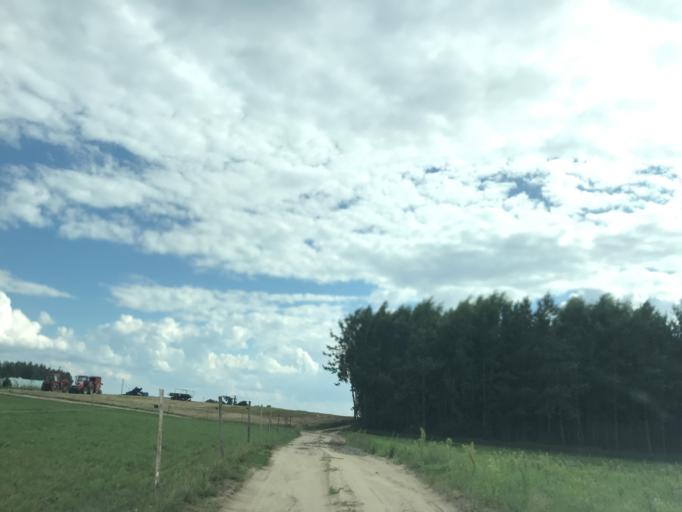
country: PL
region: Kujawsko-Pomorskie
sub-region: Powiat brodnicki
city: Brzozie
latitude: 53.3223
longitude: 19.6883
